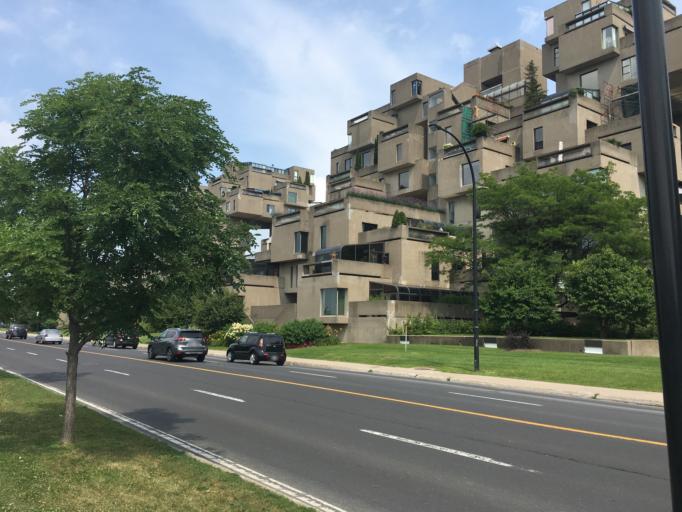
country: CA
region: Quebec
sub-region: Monteregie
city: Longueuil
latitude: 45.4997
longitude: -73.5445
